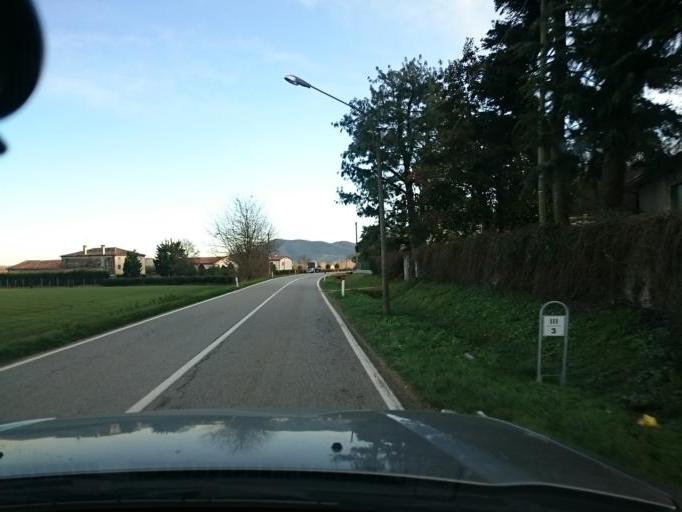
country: IT
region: Veneto
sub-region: Provincia di Padova
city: Torreglia
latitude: 45.3486
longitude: 11.7370
